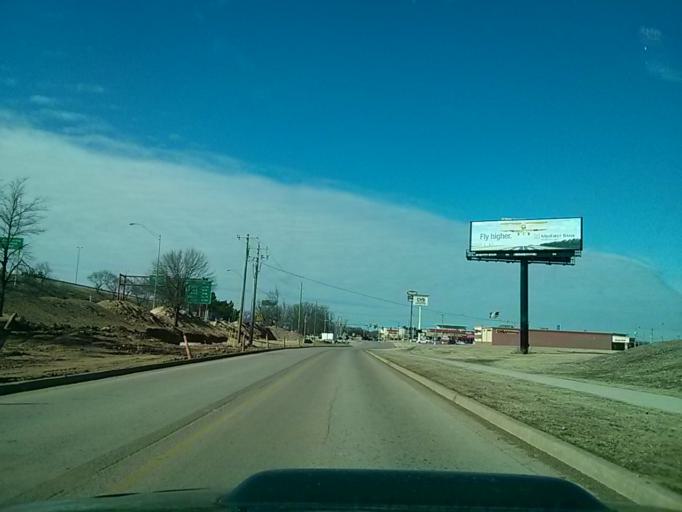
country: US
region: Oklahoma
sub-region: Tulsa County
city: Jenks
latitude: 36.0173
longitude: -95.9730
